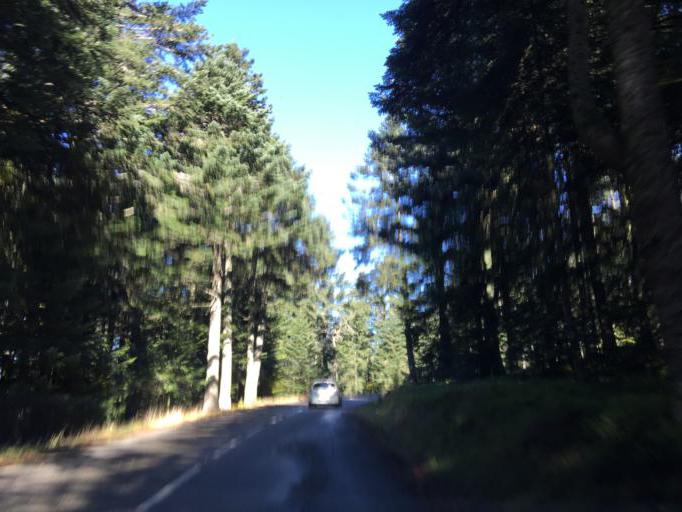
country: FR
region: Rhone-Alpes
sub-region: Departement de la Loire
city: Bourg-Argental
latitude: 45.3733
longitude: 4.5455
